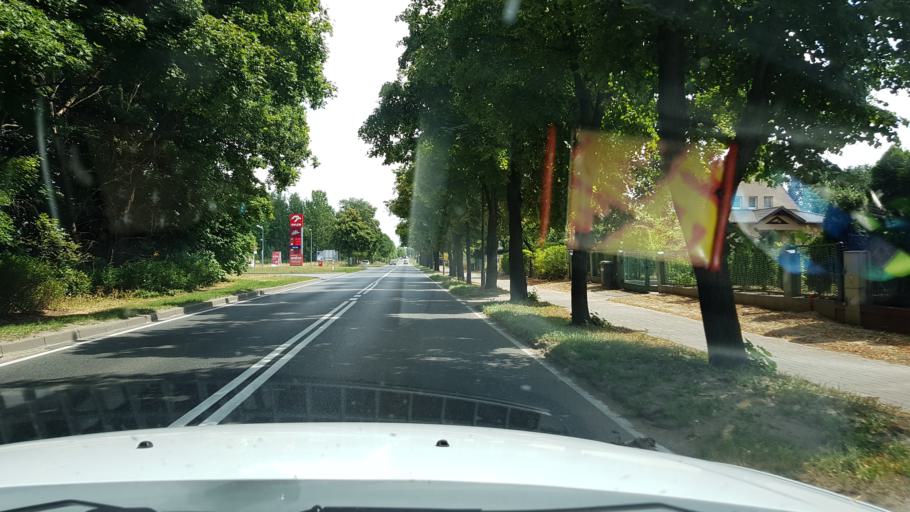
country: PL
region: West Pomeranian Voivodeship
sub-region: Powiat walecki
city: Walcz
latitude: 53.2891
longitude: 16.4371
